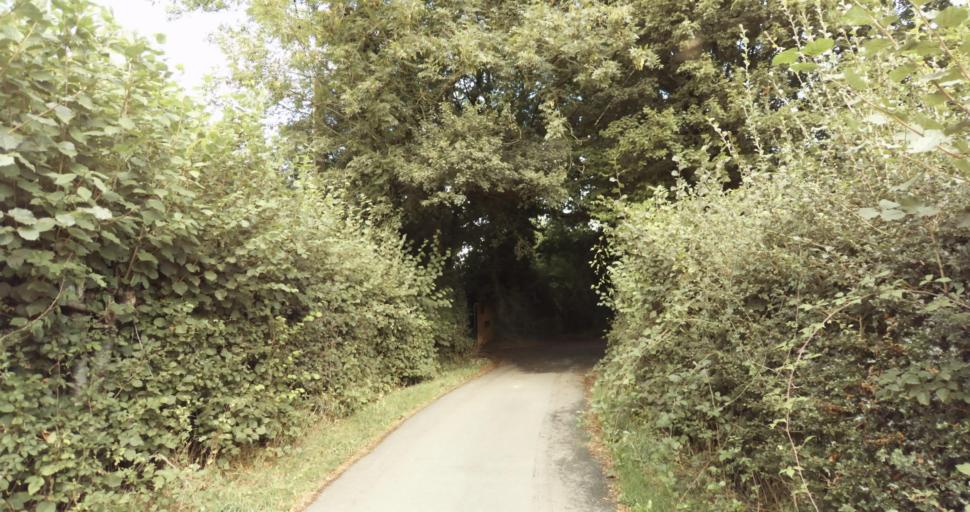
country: FR
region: Lower Normandy
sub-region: Departement de l'Orne
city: Gace
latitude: 48.7833
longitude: 0.3567
